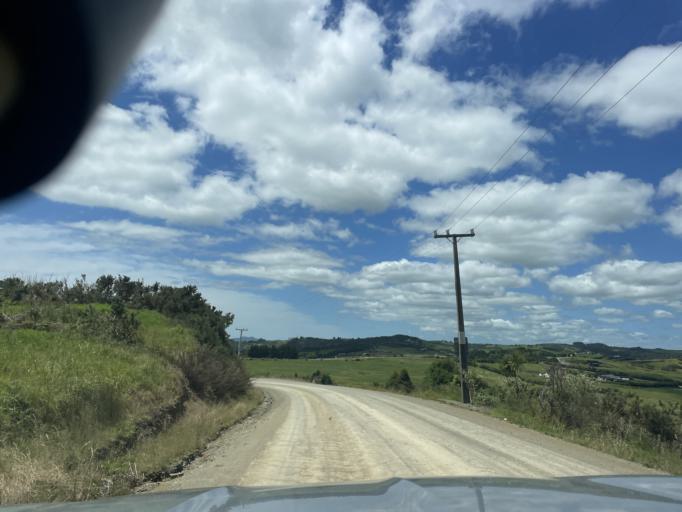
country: NZ
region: Auckland
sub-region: Auckland
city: Wellsford
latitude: -36.1454
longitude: 174.5410
